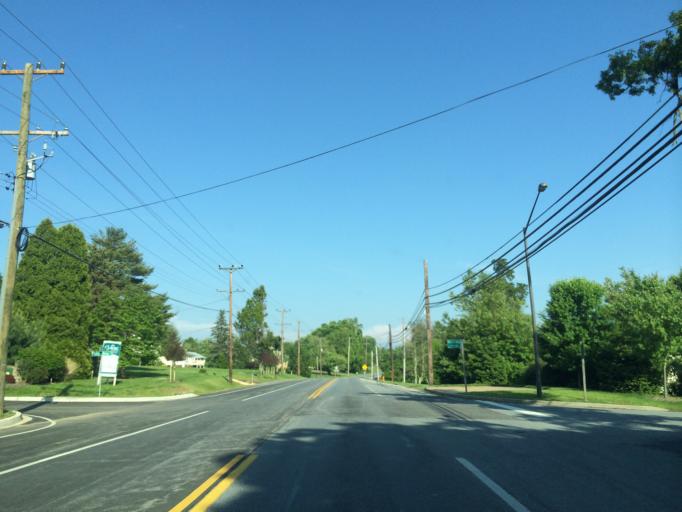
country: US
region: Maryland
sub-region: Howard County
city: Columbia
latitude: 39.2911
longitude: -76.9086
